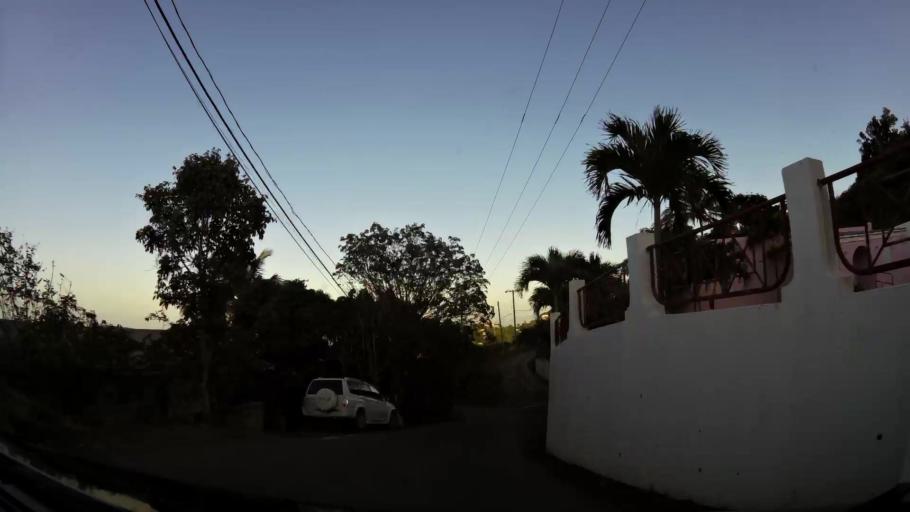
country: VG
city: Tortola
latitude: 18.4416
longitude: -64.6156
